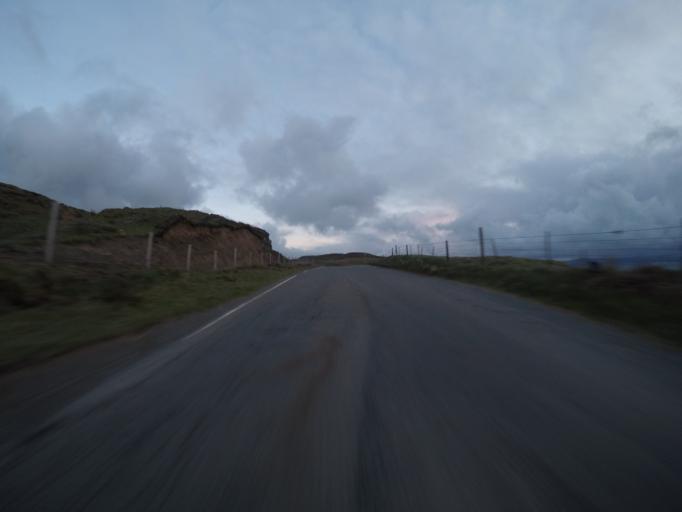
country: GB
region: Scotland
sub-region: Highland
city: Portree
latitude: 57.6045
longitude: -6.3766
